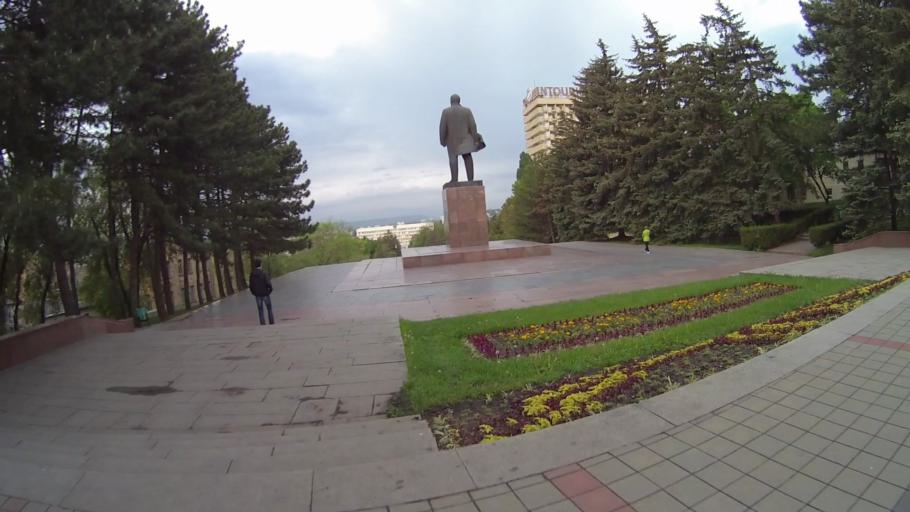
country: RU
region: Stavropol'skiy
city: Pyatigorsk
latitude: 44.0402
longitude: 43.0756
